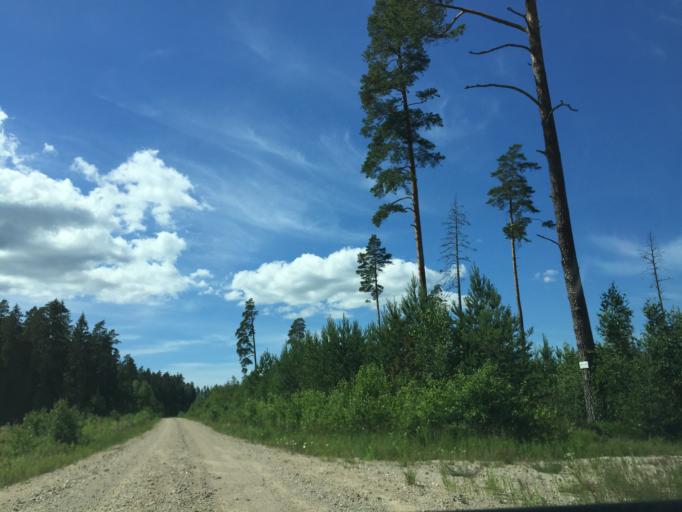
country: LV
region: Kuldigas Rajons
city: Kuldiga
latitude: 57.1099
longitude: 21.8713
